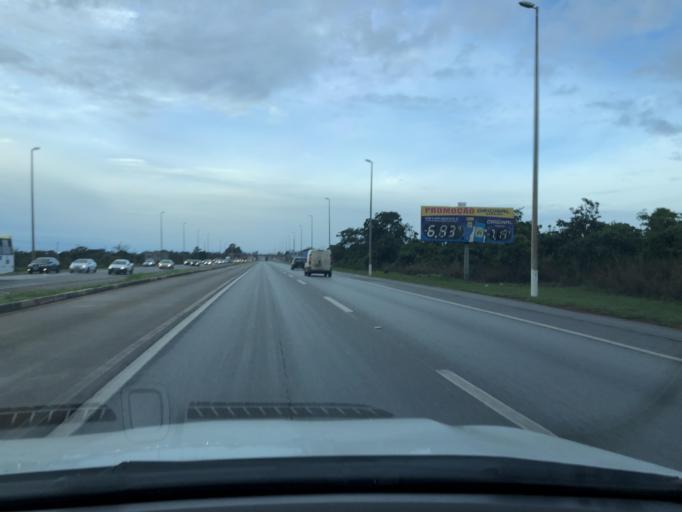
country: BR
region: Federal District
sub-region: Brasilia
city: Brasilia
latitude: -15.9860
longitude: -47.9876
